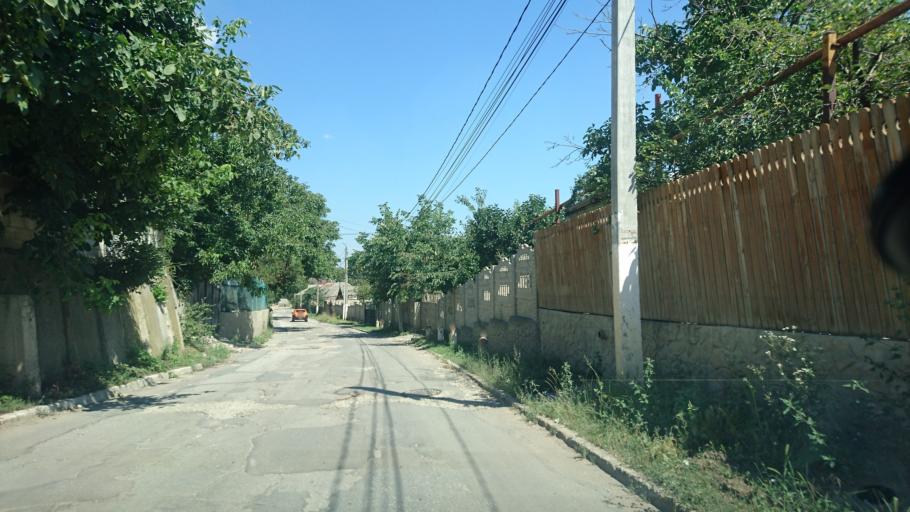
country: MD
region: Chisinau
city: Vatra
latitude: 47.0138
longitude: 28.7671
